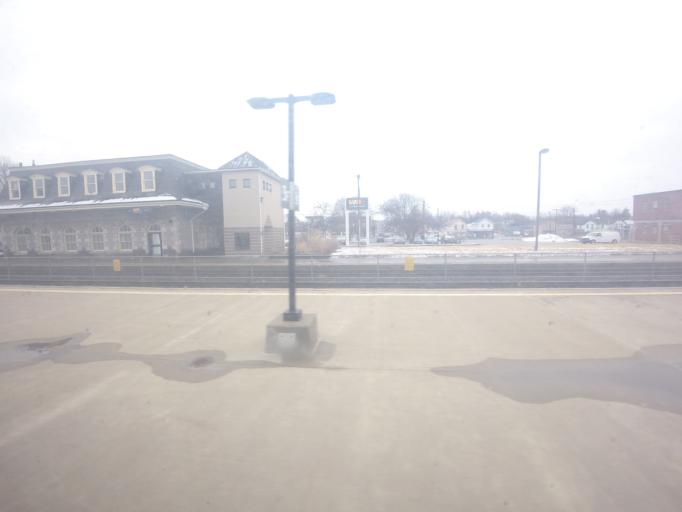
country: CA
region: Ontario
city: Belleville
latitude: 44.1795
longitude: -77.3751
